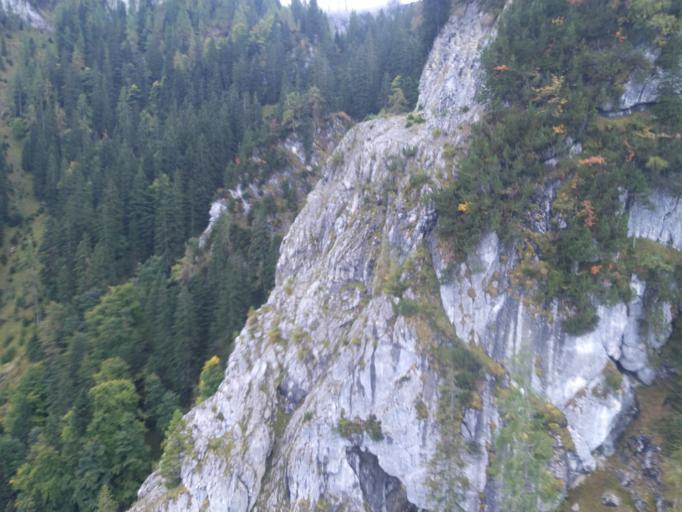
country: DE
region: Bavaria
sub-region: Upper Bavaria
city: Grainau
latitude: 47.4527
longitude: 11.0554
